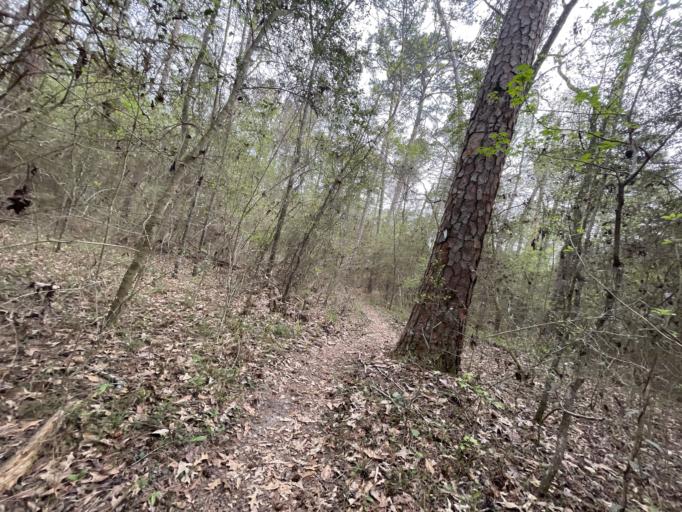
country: US
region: Texas
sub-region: Walker County
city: Huntsville
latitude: 30.6603
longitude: -95.4862
